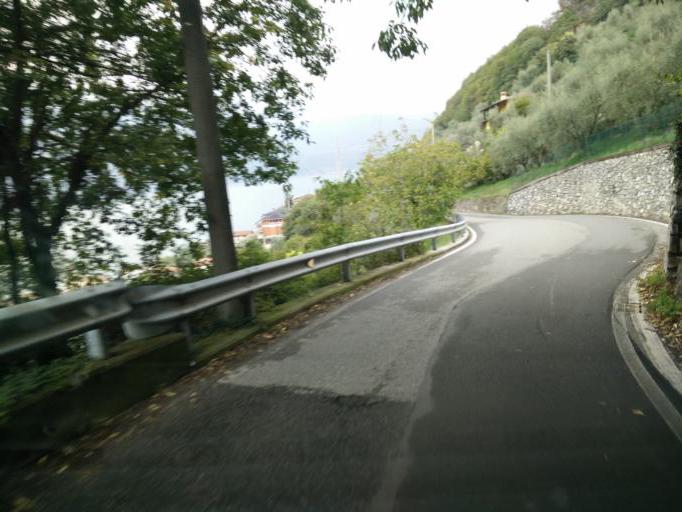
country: IT
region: Lombardy
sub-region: Provincia di Brescia
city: Marone
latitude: 45.7376
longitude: 10.0991
